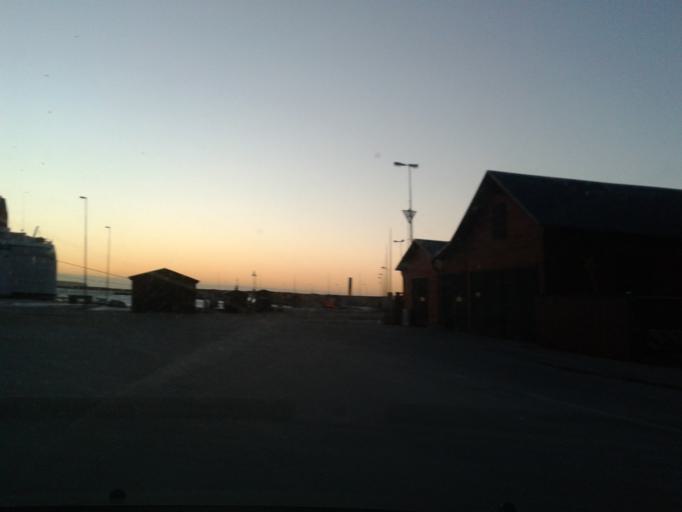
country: SE
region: Gotland
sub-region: Gotland
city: Visby
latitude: 57.6397
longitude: 18.2865
